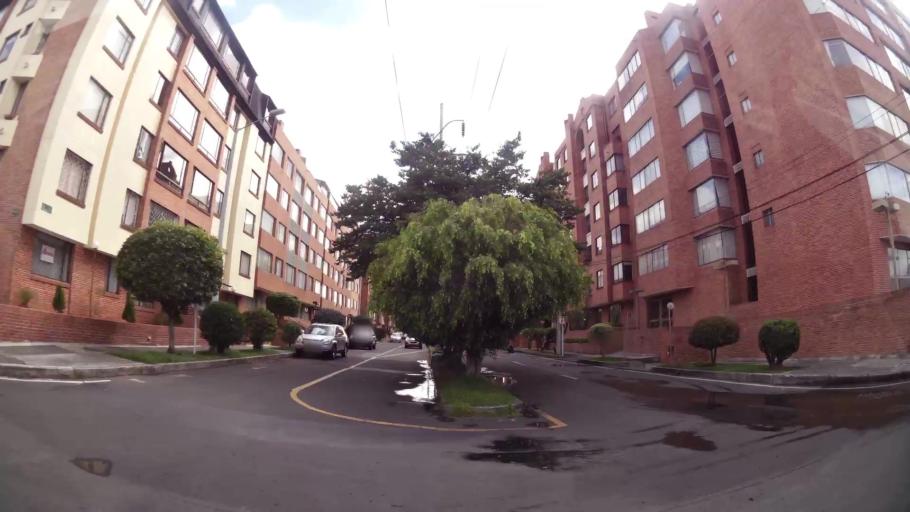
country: CO
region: Bogota D.C.
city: Barrio San Luis
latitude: 4.6976
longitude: -74.0670
